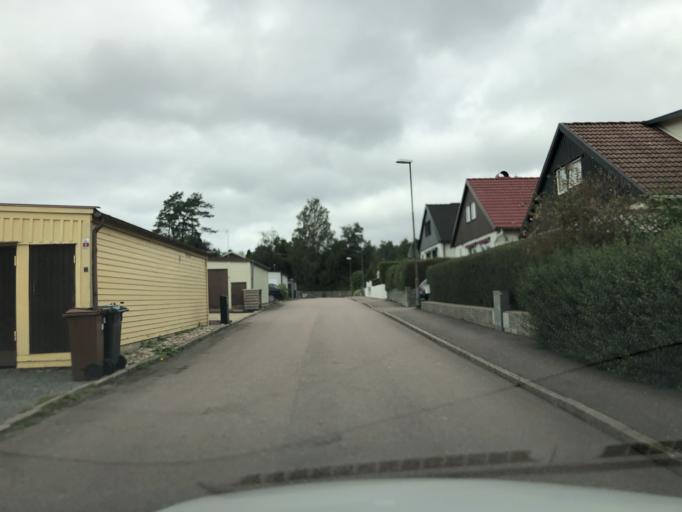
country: SE
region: Vaestra Goetaland
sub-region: Goteborg
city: Majorna
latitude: 57.7431
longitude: 11.9188
